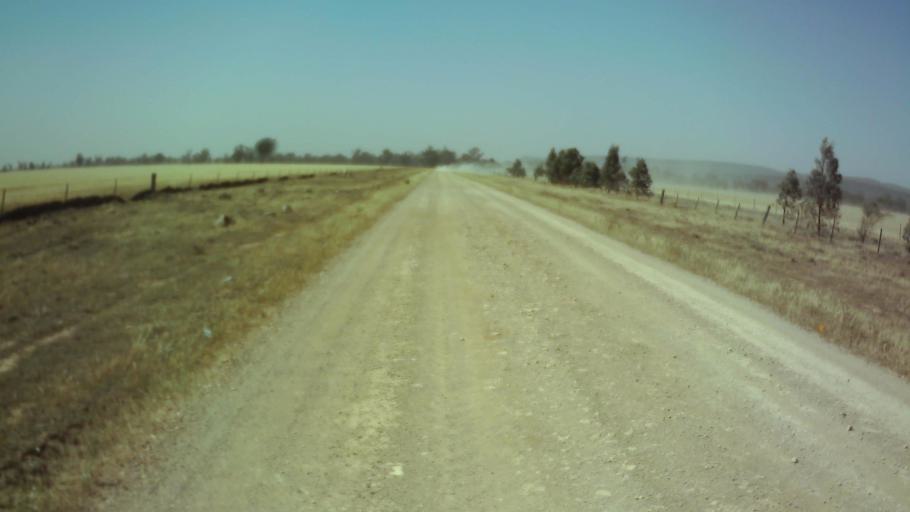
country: AU
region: New South Wales
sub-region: Weddin
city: Grenfell
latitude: -34.0111
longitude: 147.9163
